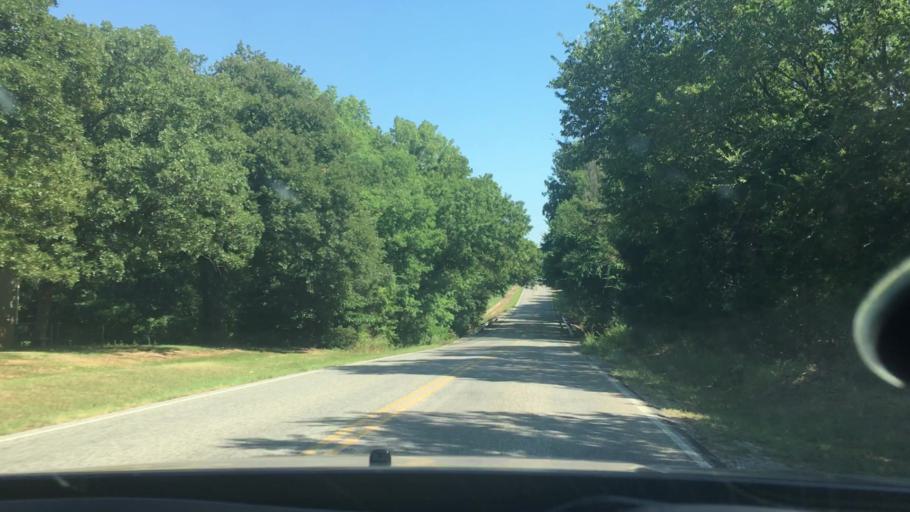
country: US
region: Oklahoma
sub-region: Johnston County
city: Tishomingo
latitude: 34.2636
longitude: -96.6186
